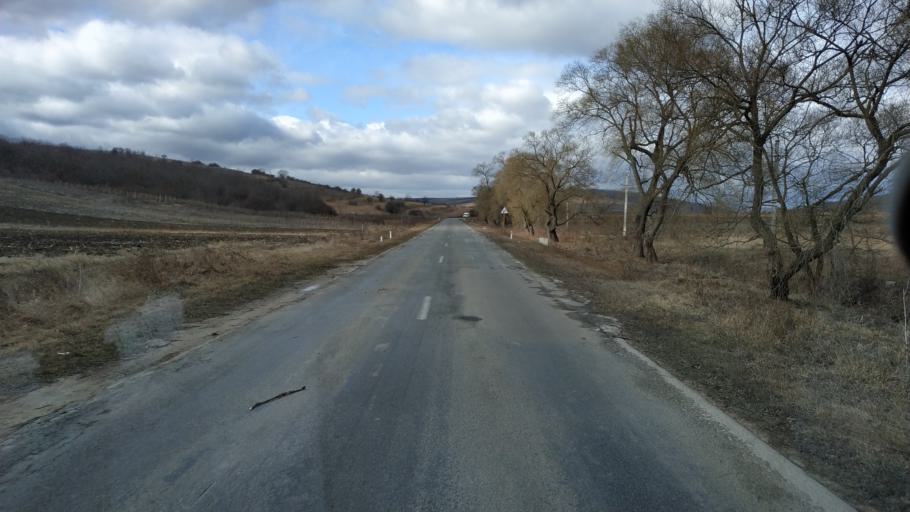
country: MD
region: Stinga Nistrului
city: Bucovat
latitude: 47.1427
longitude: 28.3700
